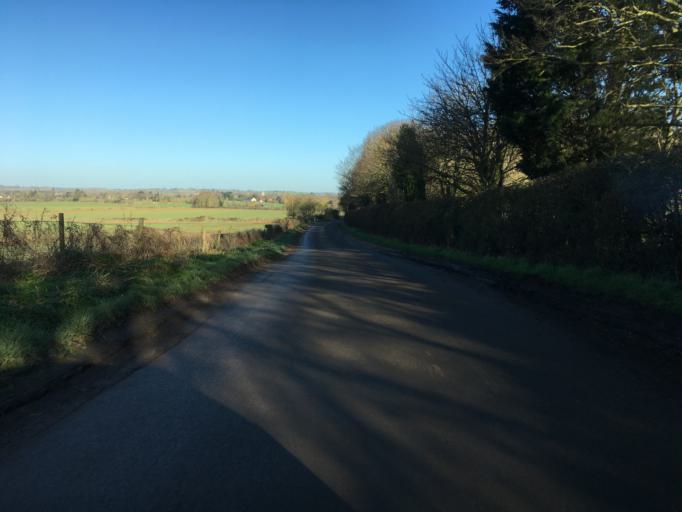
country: GB
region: England
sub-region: Warwickshire
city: Stratford-upon-Avon
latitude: 52.1922
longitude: -1.6670
